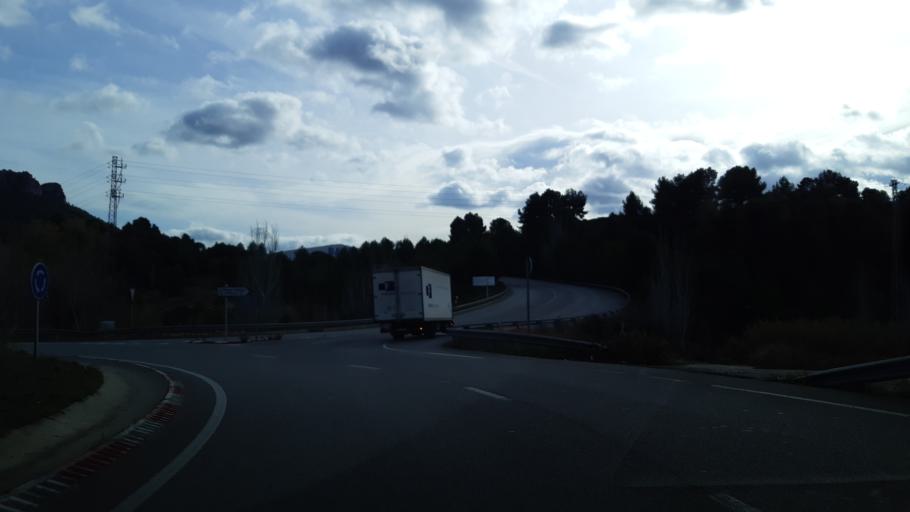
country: ES
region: Catalonia
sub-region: Provincia de Barcelona
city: La Pobla de Claramunt
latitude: 41.5761
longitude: 1.6642
